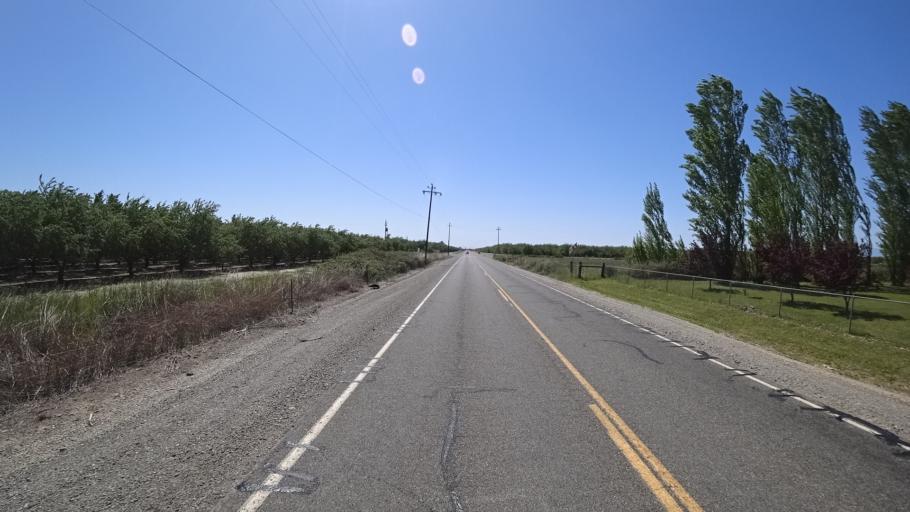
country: US
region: California
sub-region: Glenn County
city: Orland
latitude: 39.7334
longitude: -122.1409
